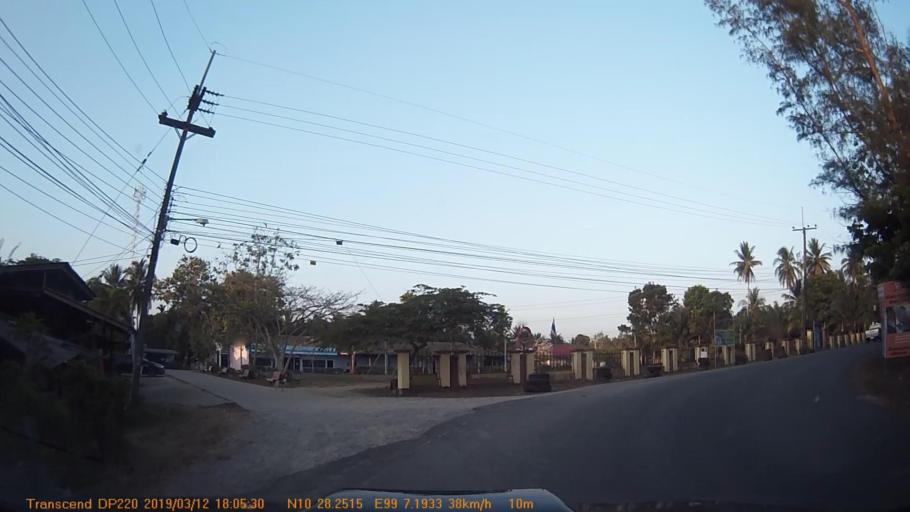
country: TH
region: Chumphon
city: Chumphon
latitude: 10.4710
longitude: 99.1200
